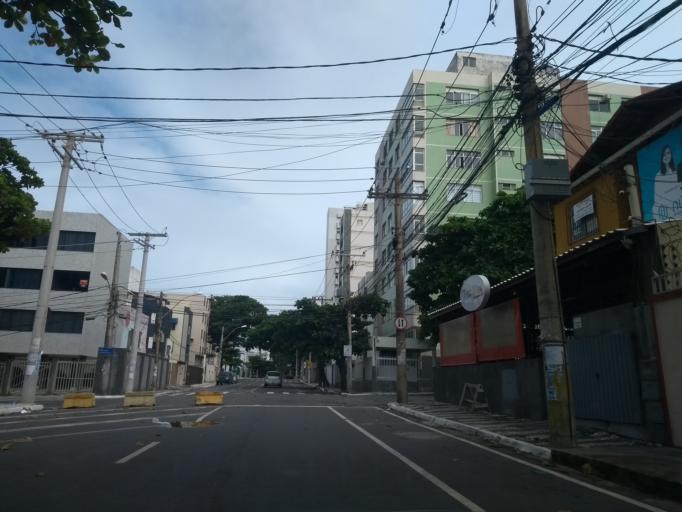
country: BR
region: Bahia
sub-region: Salvador
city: Salvador
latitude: -13.0032
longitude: -38.4536
